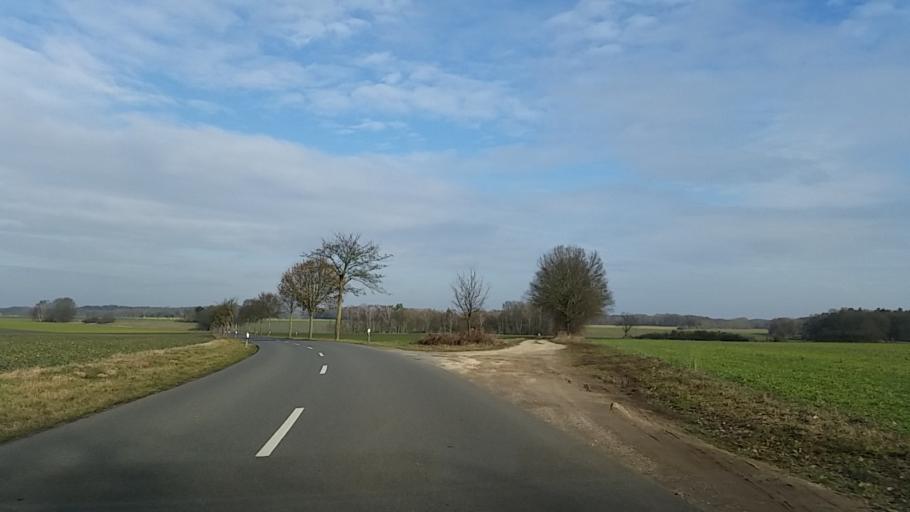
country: DE
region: Lower Saxony
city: Altenmedingen
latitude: 53.1509
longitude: 10.6194
